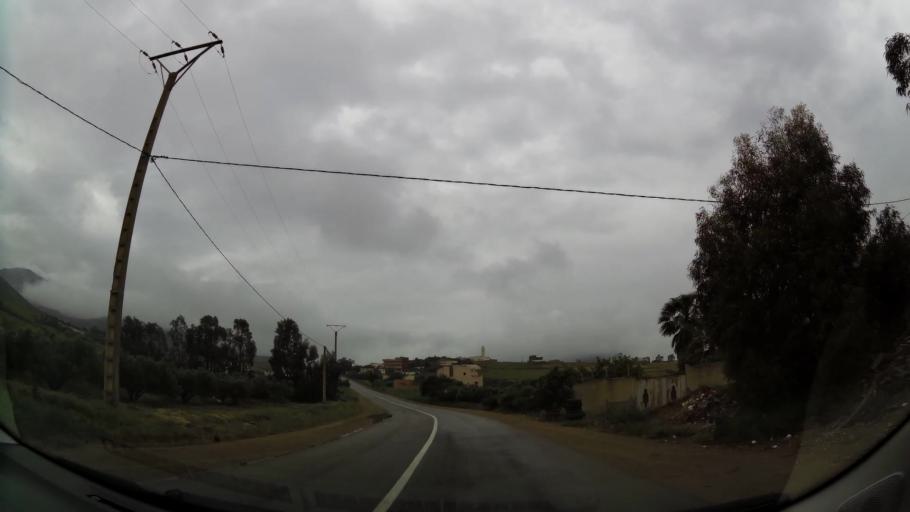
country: MA
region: Oriental
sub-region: Nador
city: Nador
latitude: 35.1458
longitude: -3.0430
